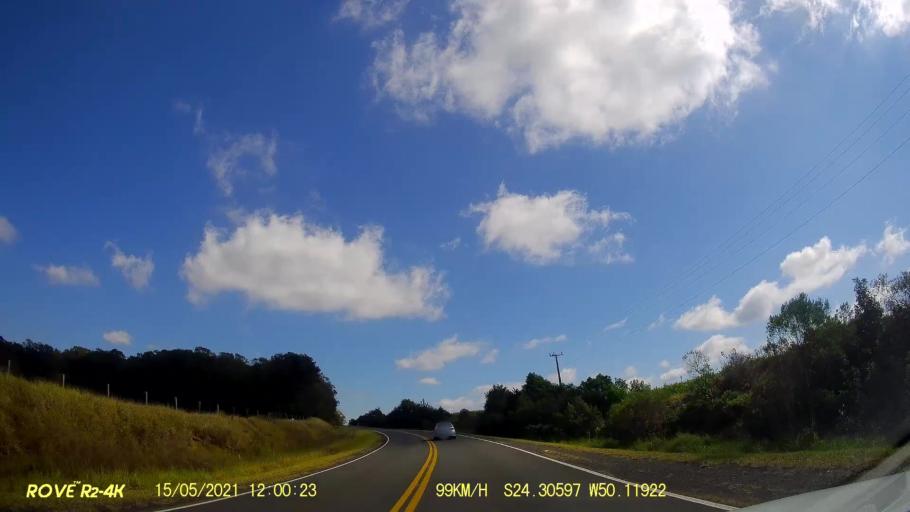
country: BR
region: Parana
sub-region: Pirai Do Sul
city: Pirai do Sul
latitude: -24.3066
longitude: -50.1192
